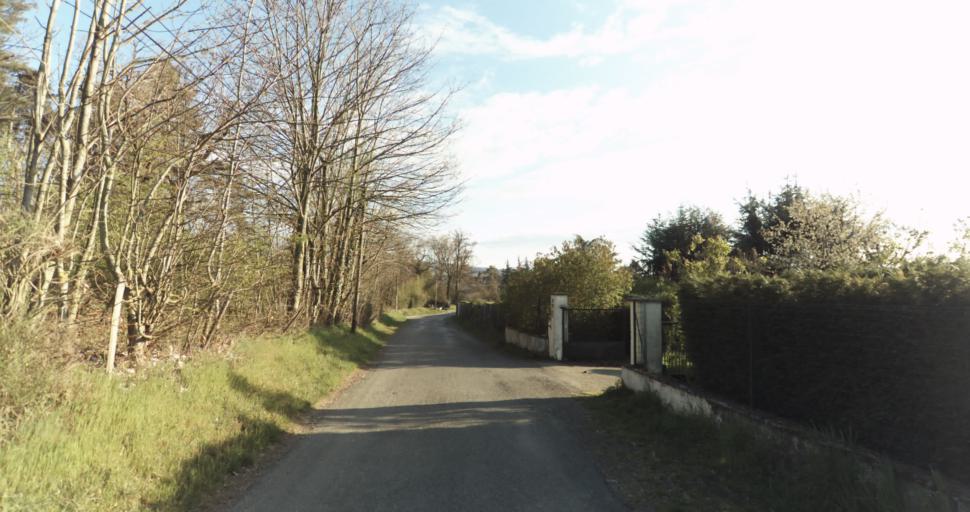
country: FR
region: Rhone-Alpes
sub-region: Departement de la Loire
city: Saint-Jean-Bonnefonds
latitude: 45.4626
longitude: 4.4462
